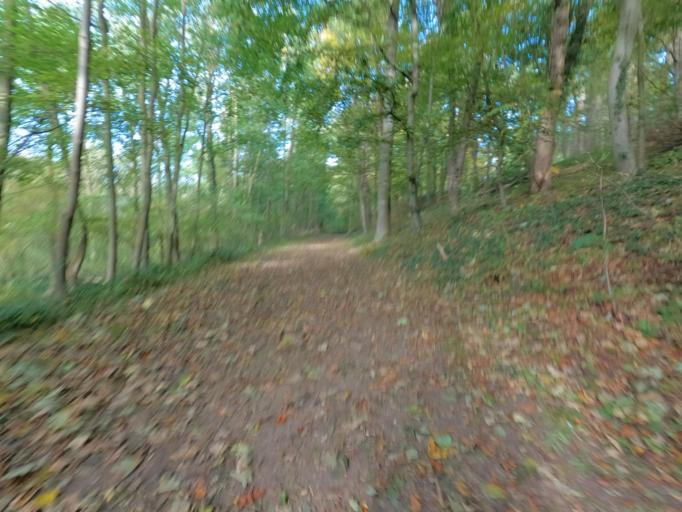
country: DE
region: North Rhine-Westphalia
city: Erkelenz
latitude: 51.0375
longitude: 6.3038
